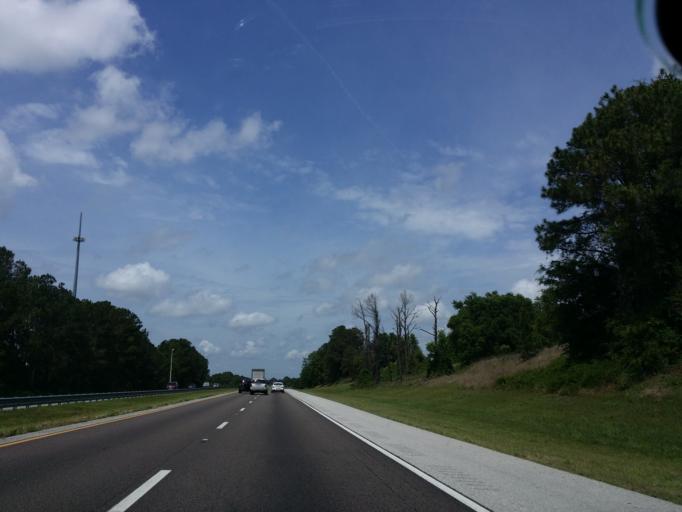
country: US
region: Florida
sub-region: Lake County
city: Minneola
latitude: 28.6363
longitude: -81.7790
